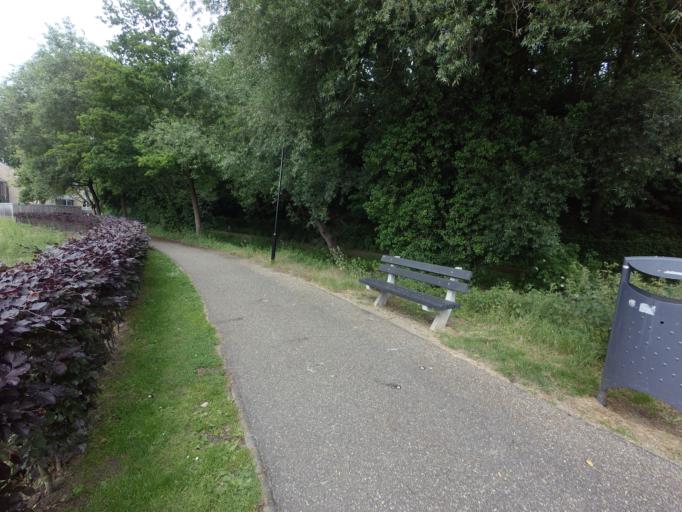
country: NL
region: Limburg
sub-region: Gemeente Simpelveld
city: Simpelveld
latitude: 50.8360
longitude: 5.9853
